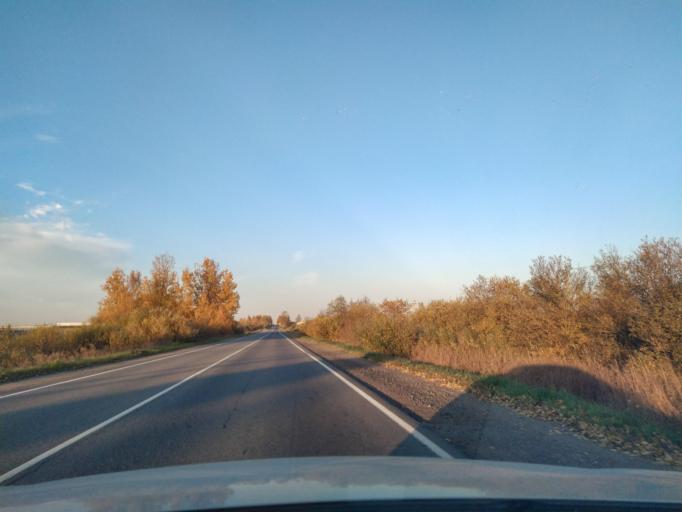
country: RU
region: Leningrad
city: Maloye Verevo
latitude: 59.6054
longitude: 30.1870
